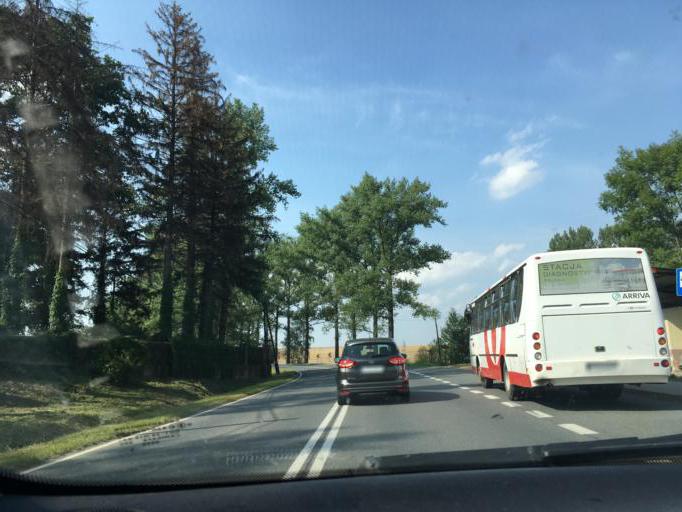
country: PL
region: Opole Voivodeship
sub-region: Powiat prudnicki
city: Laka Prudnicka
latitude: 50.3838
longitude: 17.5247
